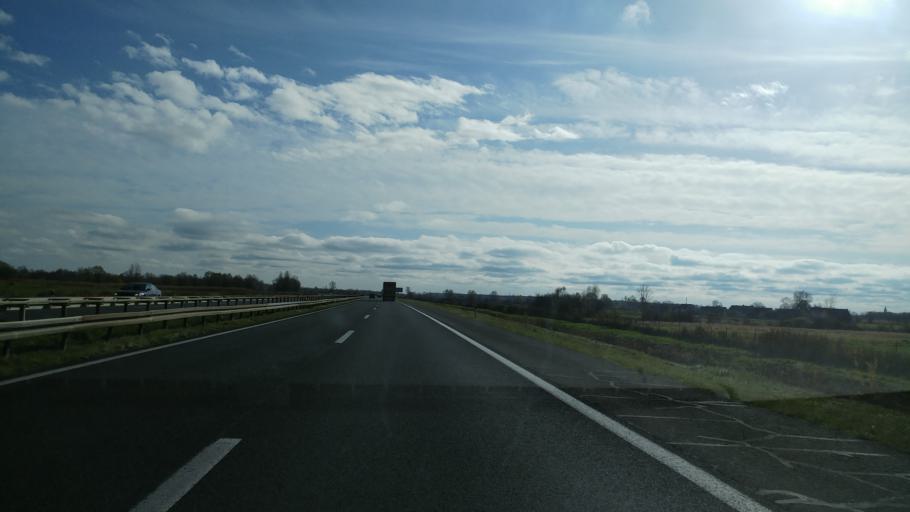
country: HR
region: Zagrebacka
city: Lupoglav
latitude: 45.7036
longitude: 16.3581
